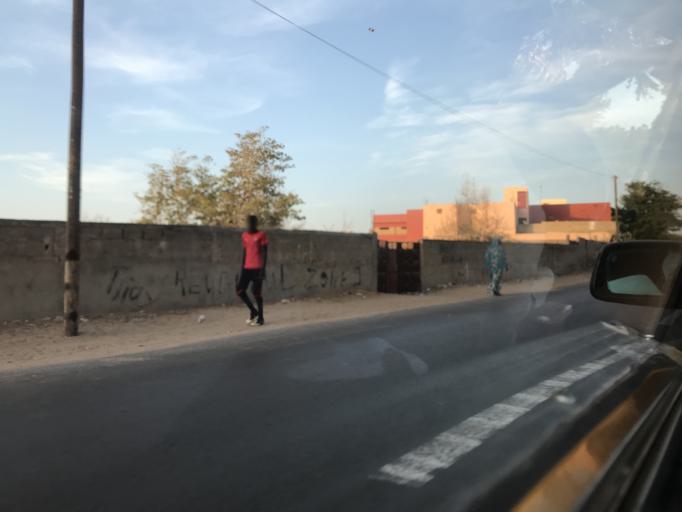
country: SN
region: Saint-Louis
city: Saint-Louis
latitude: 16.0402
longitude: -16.4448
